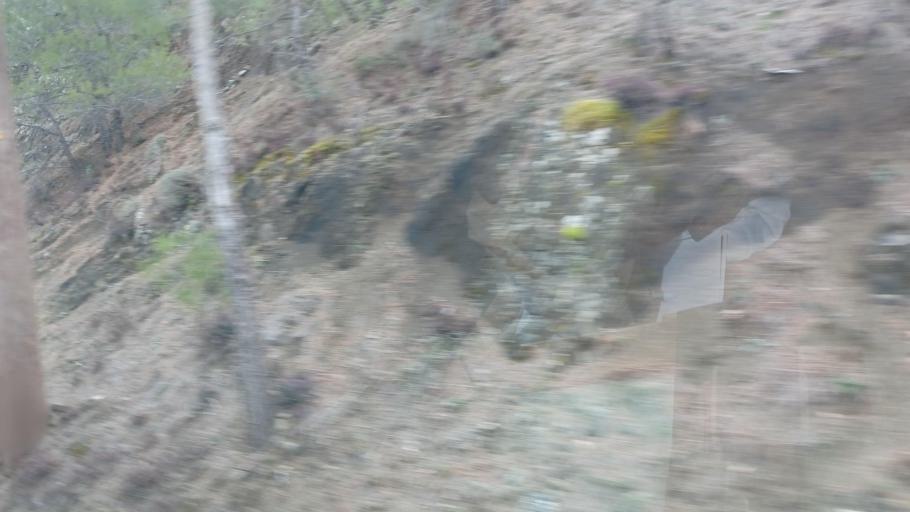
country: CY
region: Limassol
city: Pachna
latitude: 34.8734
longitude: 32.7999
